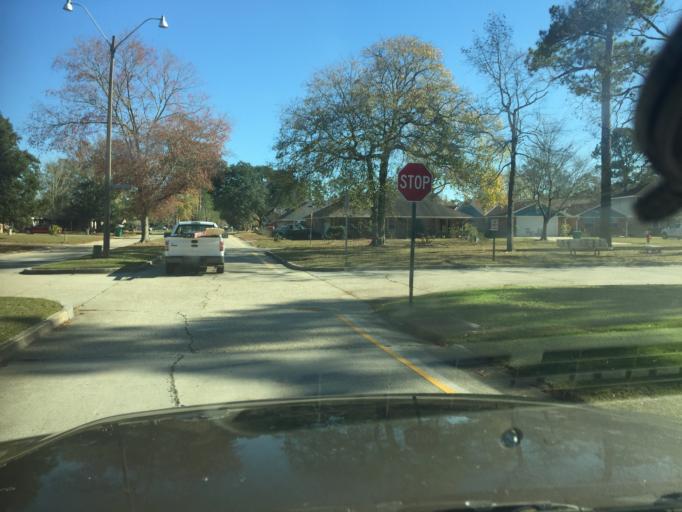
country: US
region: Louisiana
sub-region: Saint Tammany Parish
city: Slidell
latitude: 30.2996
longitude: -89.7404
